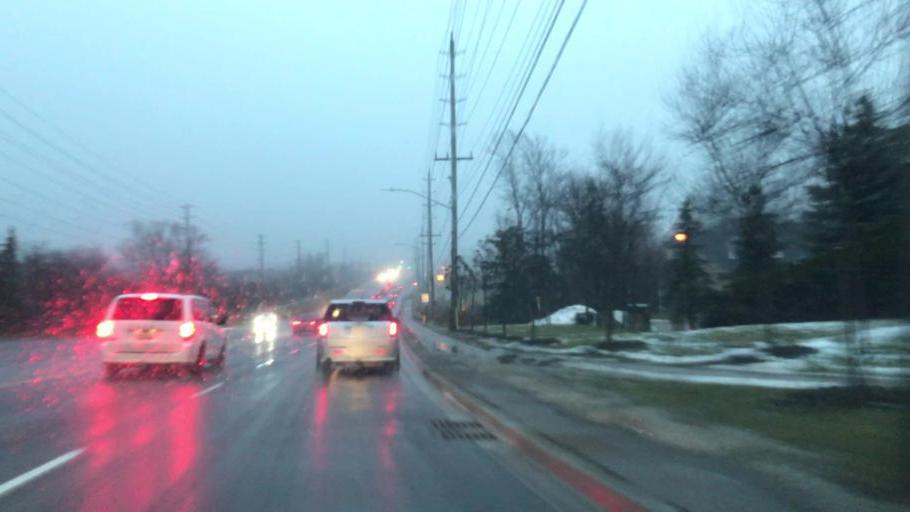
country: CA
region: Ontario
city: Newmarket
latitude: 44.0429
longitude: -79.4463
